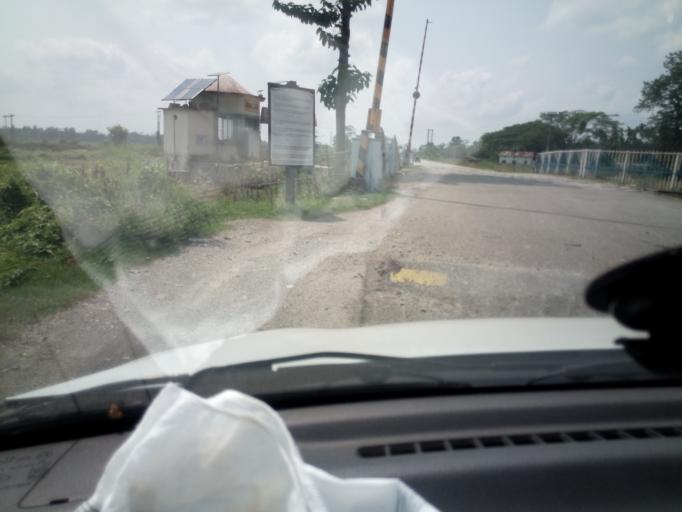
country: IN
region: Assam
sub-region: Udalguri
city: Udalguri
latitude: 26.7352
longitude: 92.1670
